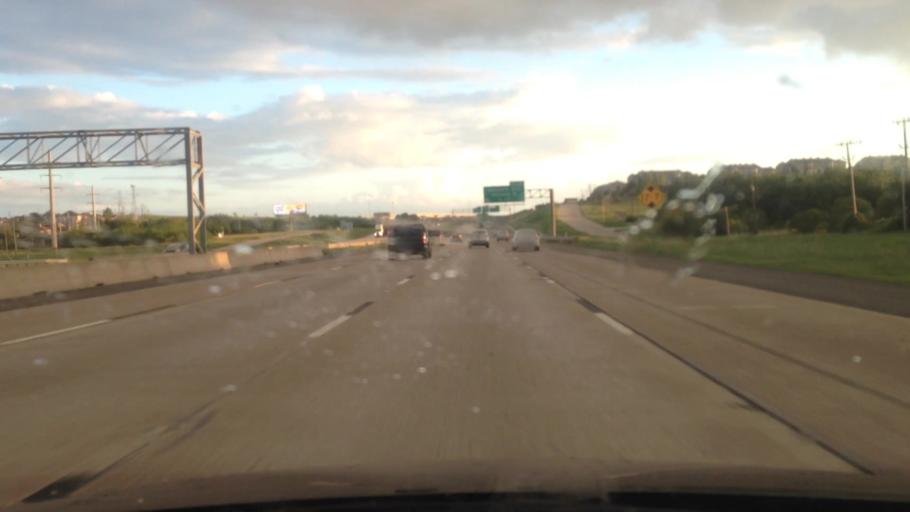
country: US
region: Texas
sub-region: Tarrant County
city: White Settlement
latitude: 32.7534
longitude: -97.4799
